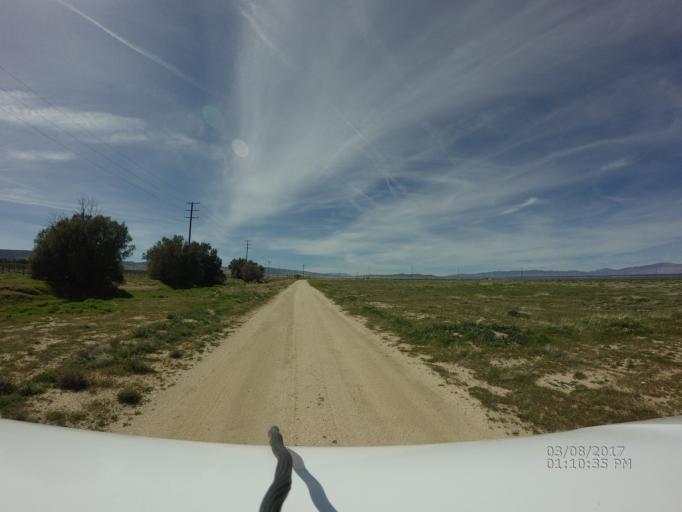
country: US
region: California
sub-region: Los Angeles County
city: Leona Valley
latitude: 34.7185
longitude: -118.3049
